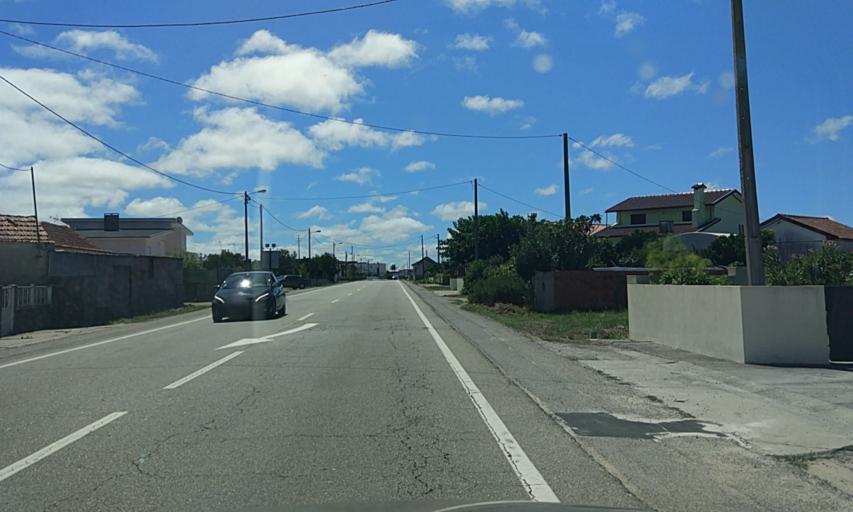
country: PT
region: Aveiro
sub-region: Vagos
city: Vagos
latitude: 40.4881
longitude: -8.6874
